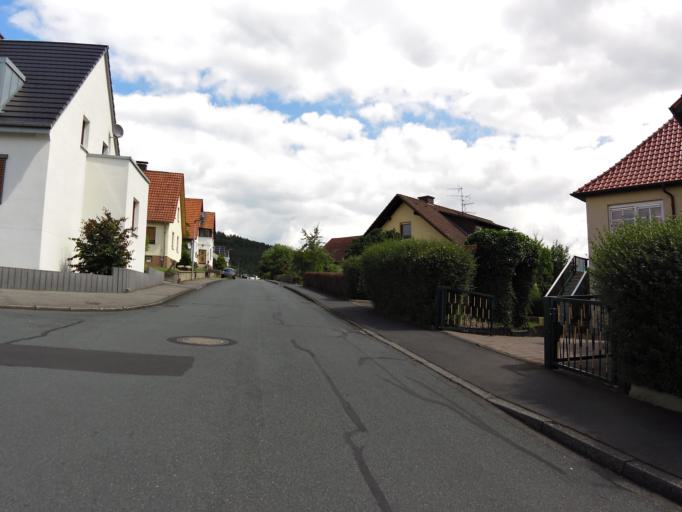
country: DE
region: Hesse
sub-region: Regierungsbezirk Kassel
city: Herleshausen
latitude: 51.0048
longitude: 10.1695
